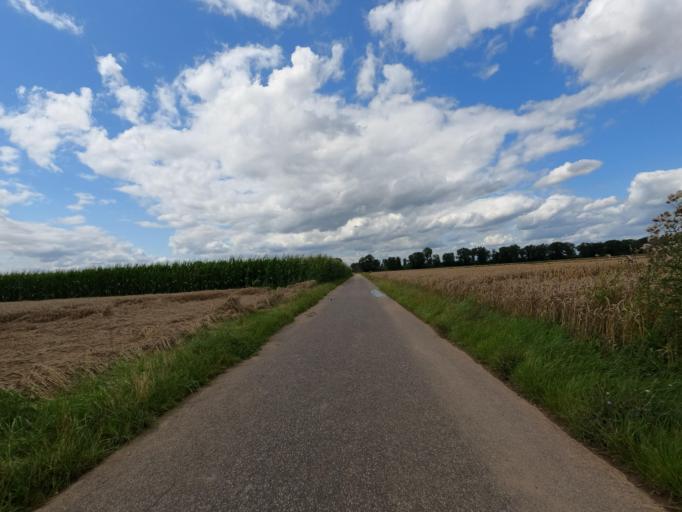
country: DE
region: North Rhine-Westphalia
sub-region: Regierungsbezirk Koln
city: Linnich
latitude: 51.0126
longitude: 6.2471
